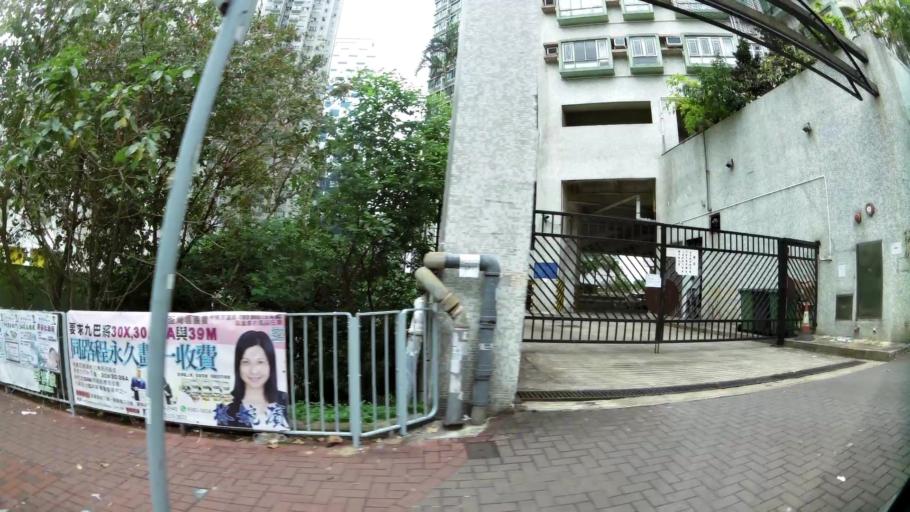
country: HK
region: Tsuen Wan
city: Tsuen Wan
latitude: 22.3765
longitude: 114.1063
